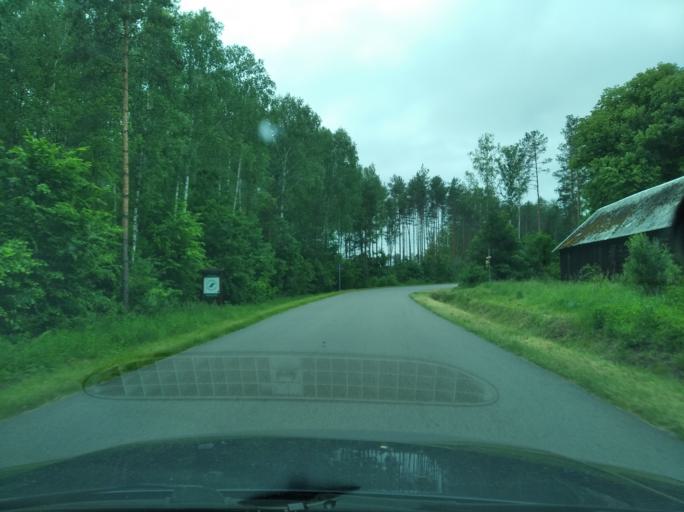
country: PL
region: Subcarpathian Voivodeship
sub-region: Powiat kolbuszowski
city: Niwiska
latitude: 50.2015
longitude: 21.6534
